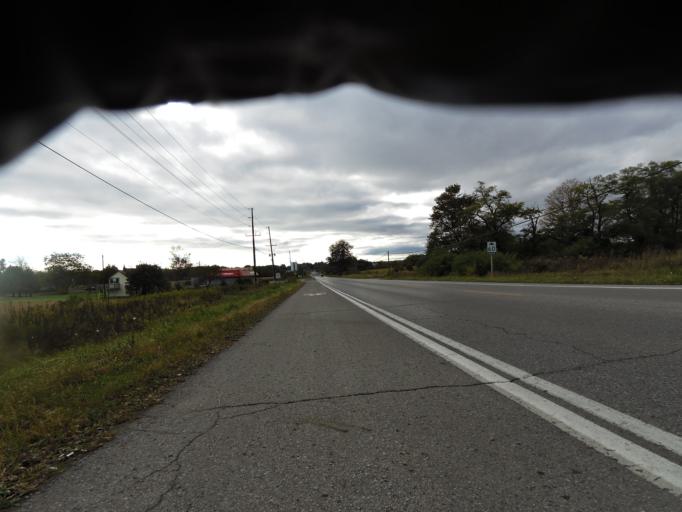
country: CA
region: Ontario
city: Cobourg
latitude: 43.9570
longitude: -78.2611
